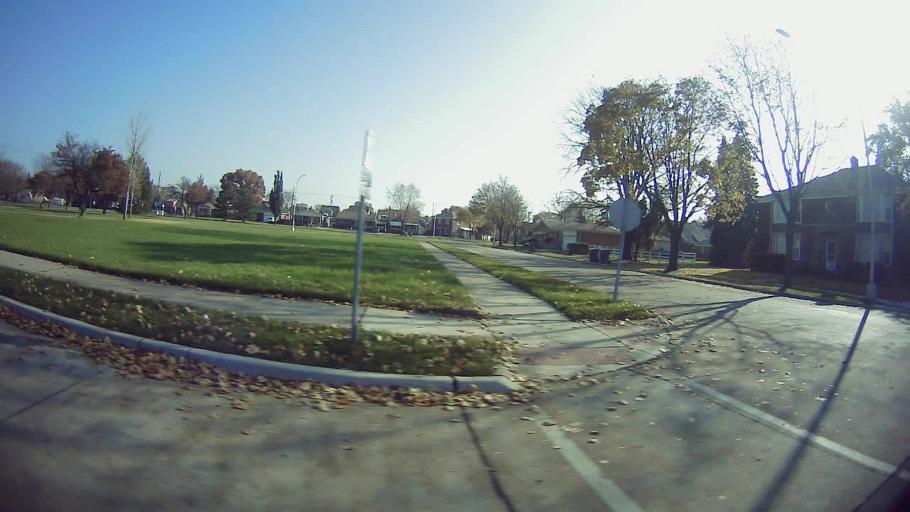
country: US
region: Michigan
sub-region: Wayne County
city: Dearborn
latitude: 42.3513
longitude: -83.1667
